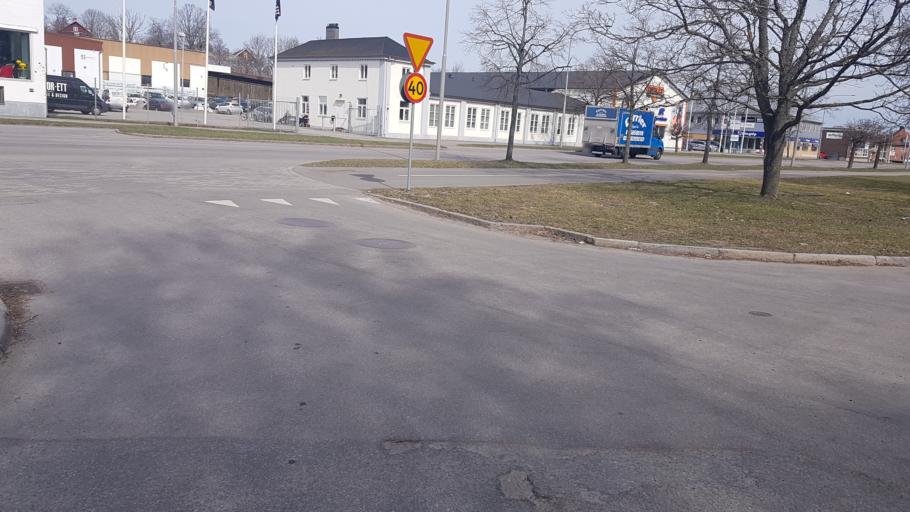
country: SE
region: OEstergoetland
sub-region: Norrkopings Kommun
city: Norrkoping
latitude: 58.5902
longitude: 16.2114
